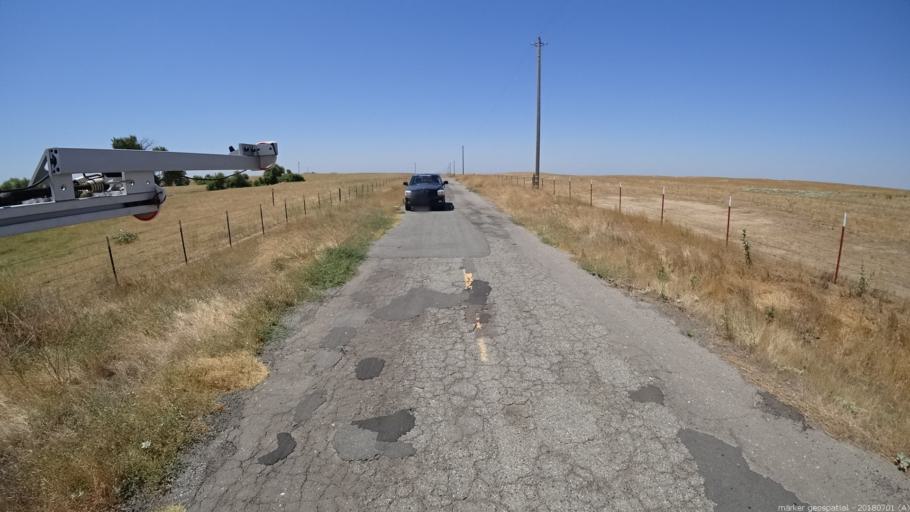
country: US
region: California
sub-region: Madera County
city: Madera Acres
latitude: 37.1116
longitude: -119.9889
